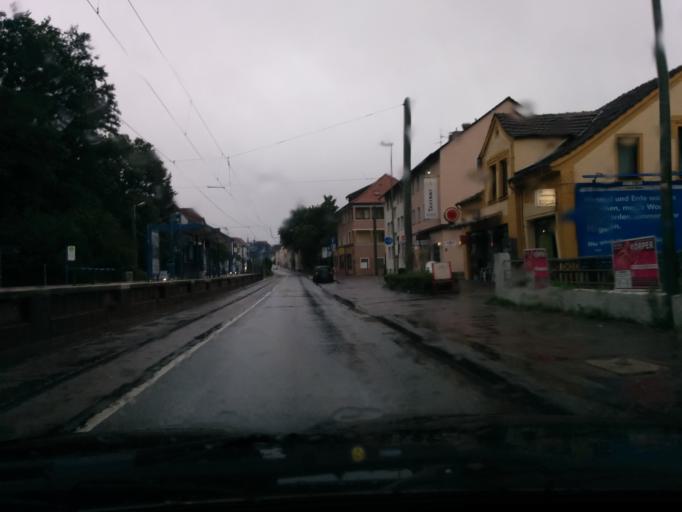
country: DE
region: North Rhine-Westphalia
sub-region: Regierungsbezirk Detmold
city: Bielefeld
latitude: 52.0416
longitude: 8.5229
